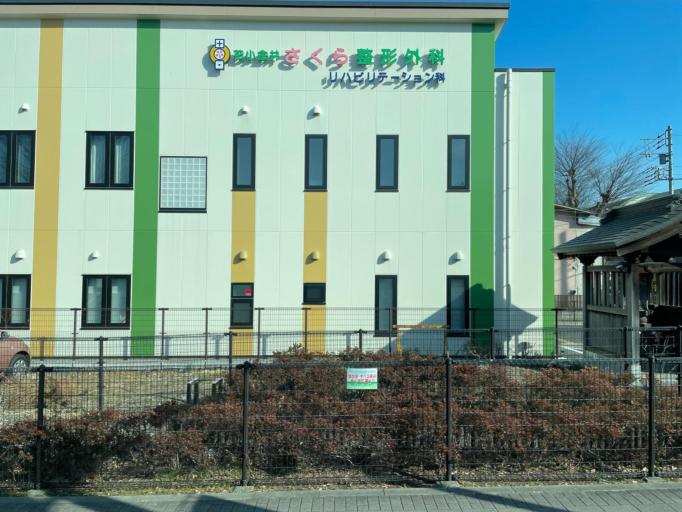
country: JP
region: Tokyo
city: Tanashicho
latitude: 35.7296
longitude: 139.5148
